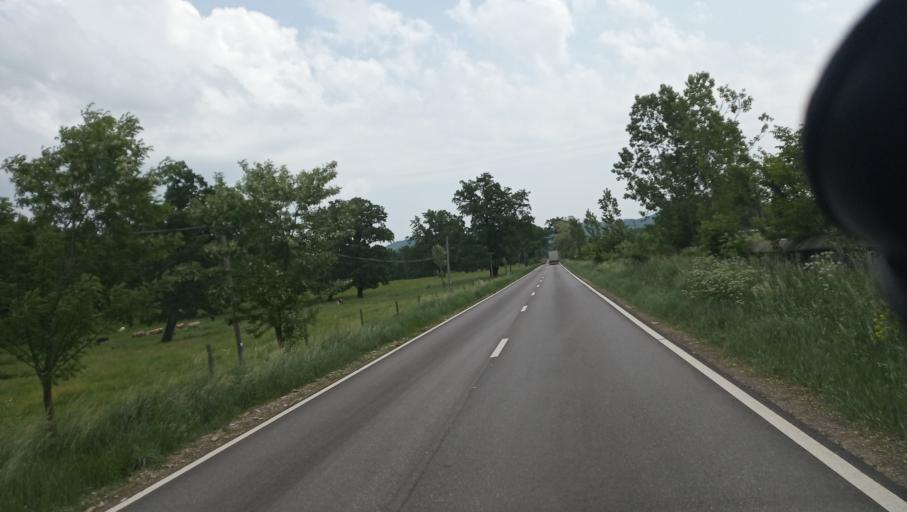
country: RO
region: Neamt
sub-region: Comuna Vanatori Neamt
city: Nemtisor
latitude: 47.2289
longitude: 26.2142
